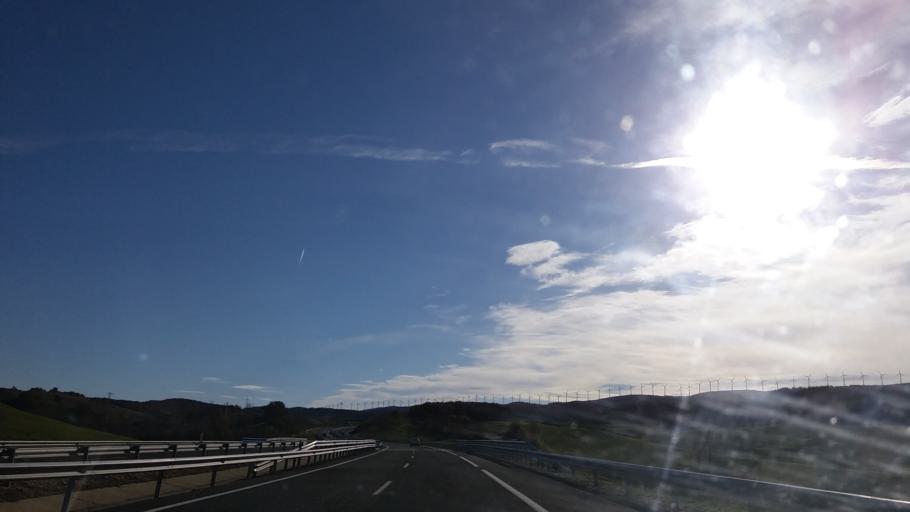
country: ES
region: Navarre
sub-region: Provincia de Navarra
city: Monreal
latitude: 42.6719
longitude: -1.4439
